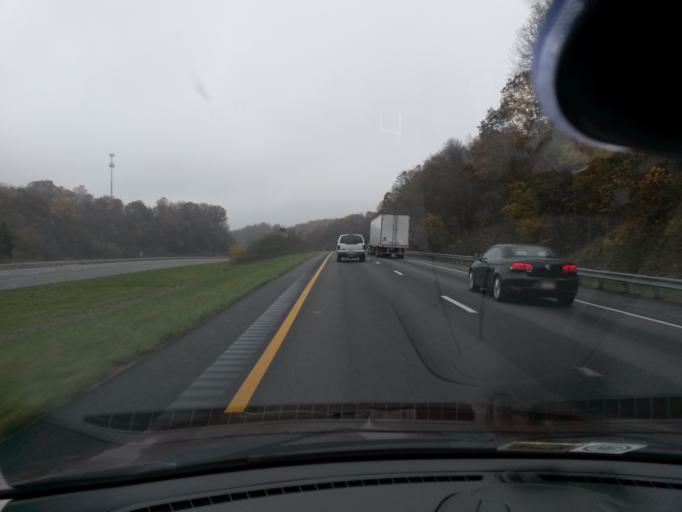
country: US
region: Virginia
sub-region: Montgomery County
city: Shawsville
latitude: 37.1696
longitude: -80.3090
